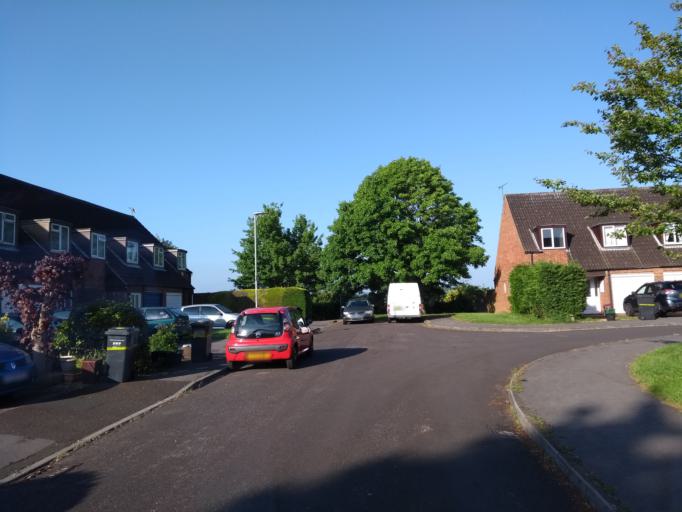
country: GB
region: England
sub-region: Somerset
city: Taunton
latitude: 51.0039
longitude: -3.0791
